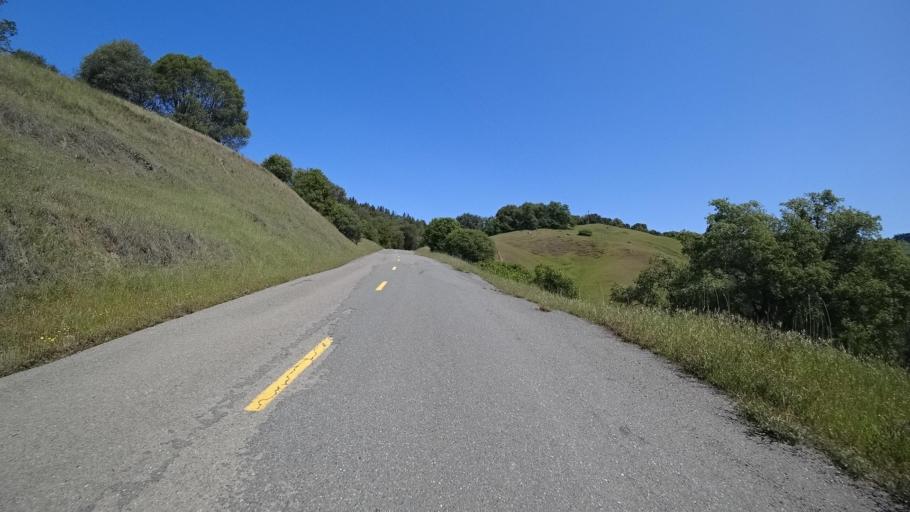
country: US
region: California
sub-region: Humboldt County
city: Redway
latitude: 40.1796
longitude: -123.5937
